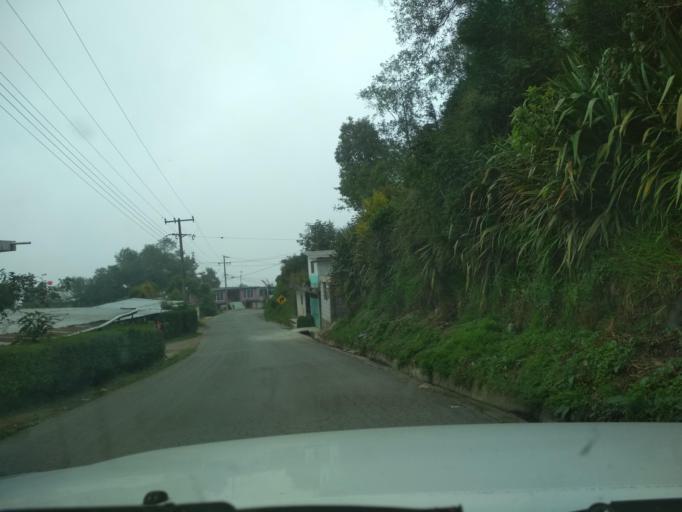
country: MX
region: Veracruz
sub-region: La Perla
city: Chilapa
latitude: 18.9735
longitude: -97.1717
